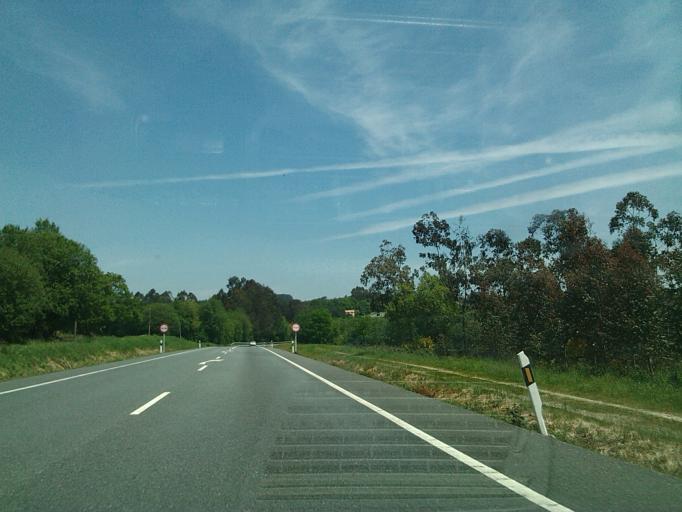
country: ES
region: Galicia
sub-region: Provincia da Coruna
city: Mesia
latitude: 43.0815
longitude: -8.1927
